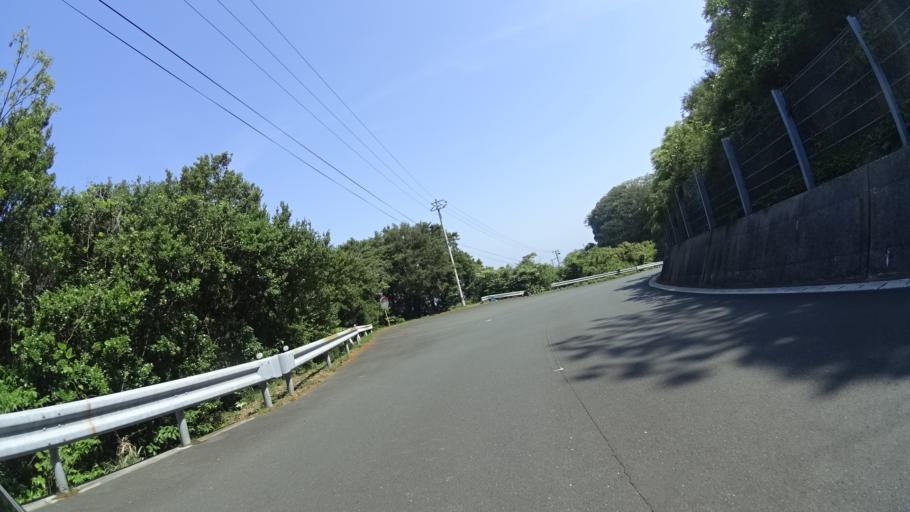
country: JP
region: Oita
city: Tsukumiura
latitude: 33.3634
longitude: 132.0394
